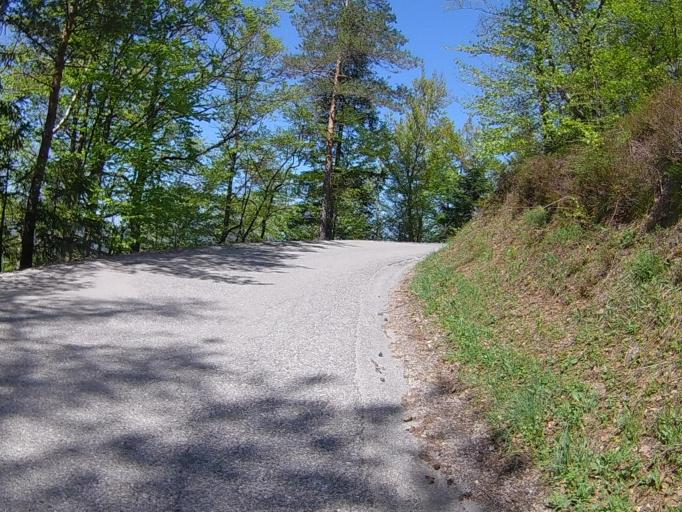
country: SI
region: Ruse
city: Ruse
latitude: 46.5247
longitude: 15.5249
